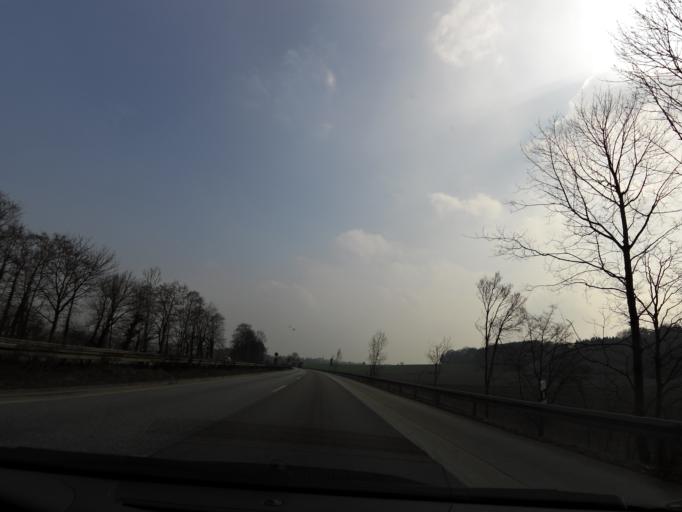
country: NL
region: Limburg
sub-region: Gemeente Vaals
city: Vaals
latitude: 50.8107
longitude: 6.0346
